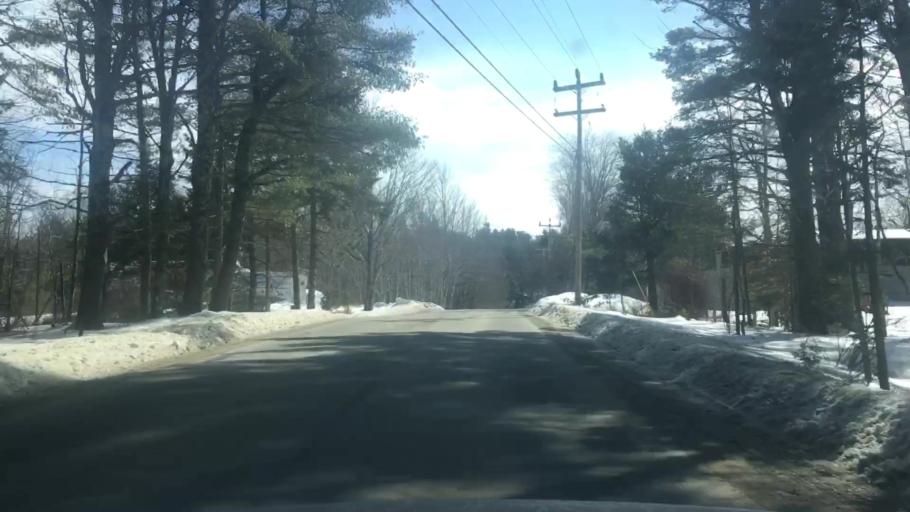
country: US
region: Maine
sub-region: Penobscot County
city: Holden
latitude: 44.7528
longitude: -68.6340
